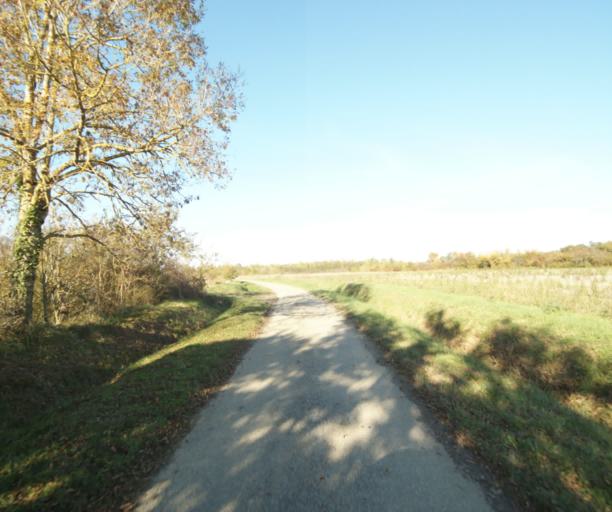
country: FR
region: Midi-Pyrenees
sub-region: Departement du Tarn-et-Garonne
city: Finhan
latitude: 43.9223
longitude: 1.2082
